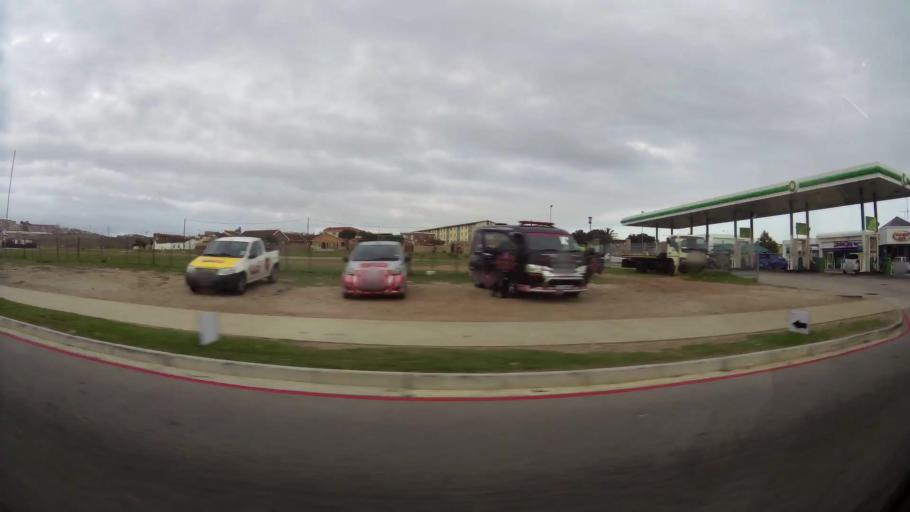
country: ZA
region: Eastern Cape
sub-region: Nelson Mandela Bay Metropolitan Municipality
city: Port Elizabeth
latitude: -33.9201
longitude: 25.5650
